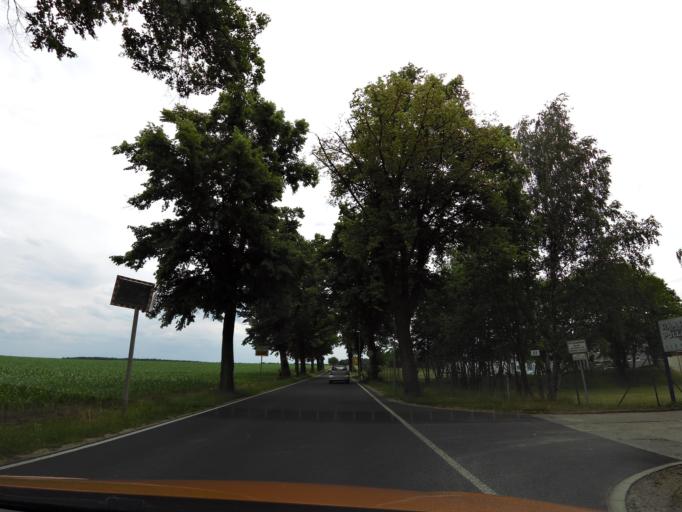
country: DE
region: Brandenburg
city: Rangsdorf
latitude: 52.2447
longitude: 13.3853
